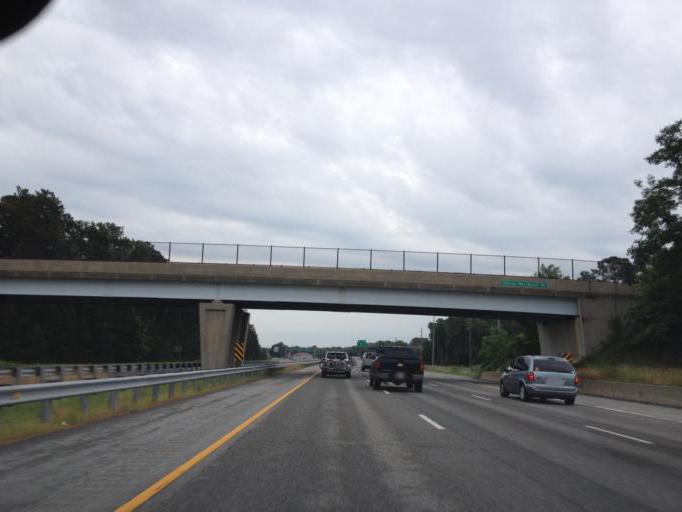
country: US
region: Maryland
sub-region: Queen Anne's County
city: Grasonville
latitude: 38.9625
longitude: -76.2118
